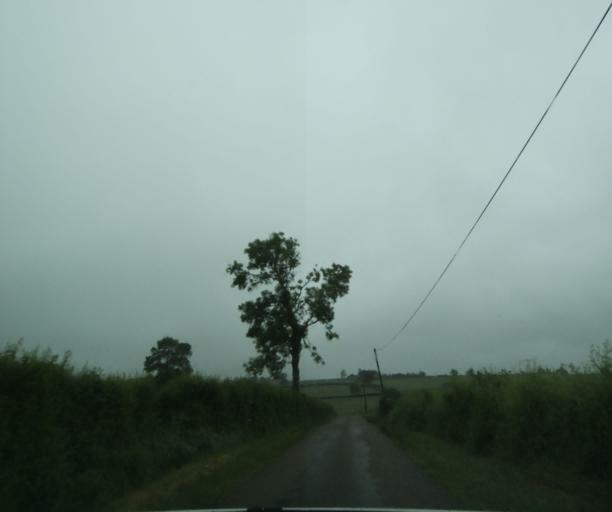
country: FR
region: Bourgogne
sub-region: Departement de Saone-et-Loire
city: Charolles
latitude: 46.4032
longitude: 4.2119
